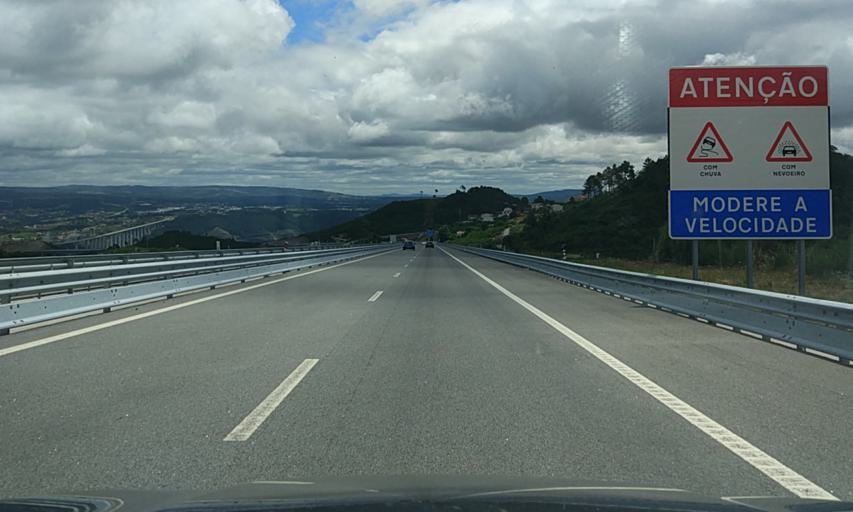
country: PT
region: Vila Real
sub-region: Santa Marta de Penaguiao
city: Santa Marta de Penaguiao
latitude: 41.2684
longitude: -7.8012
